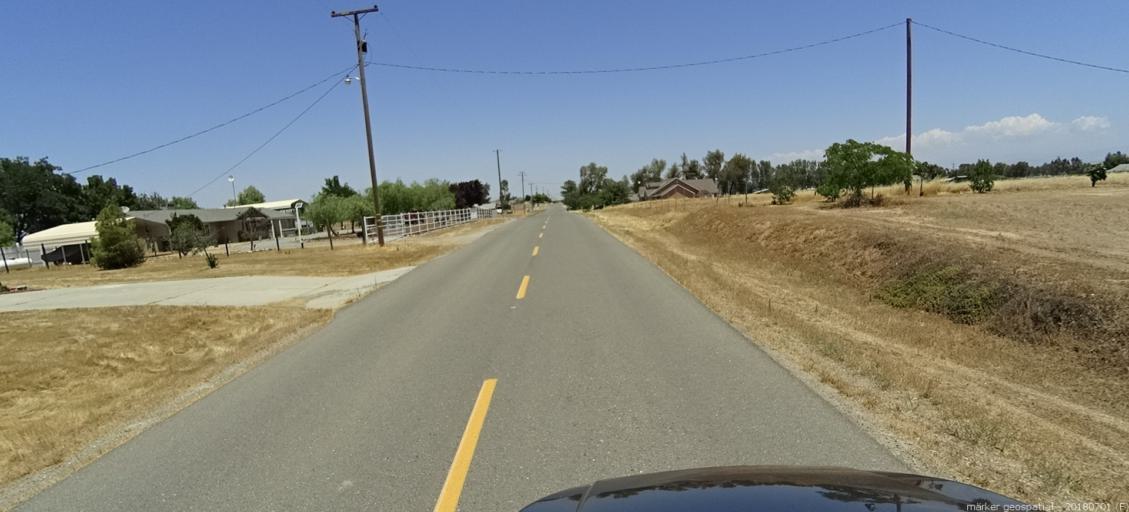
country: US
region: California
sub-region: Madera County
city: Madera Acres
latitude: 37.0369
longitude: -119.9957
